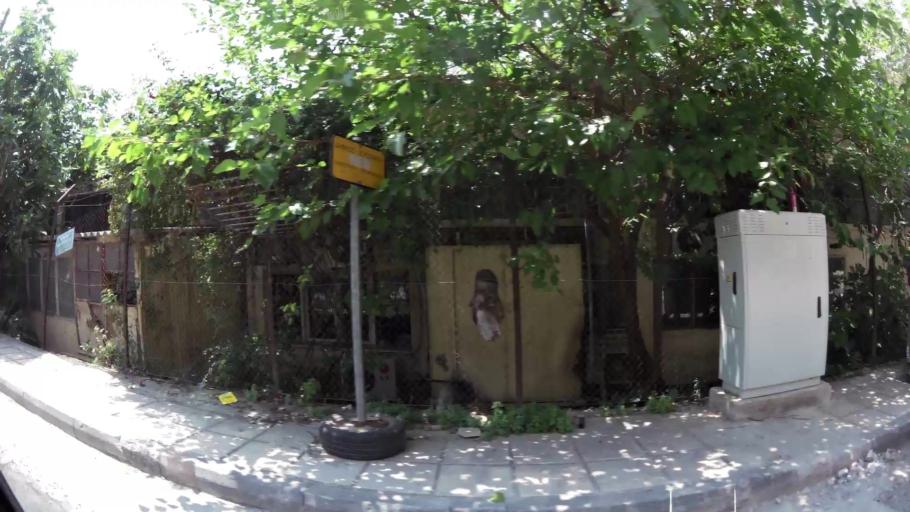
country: GR
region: Central Macedonia
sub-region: Nomos Thessalonikis
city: Evosmos
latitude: 40.6654
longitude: 22.9040
